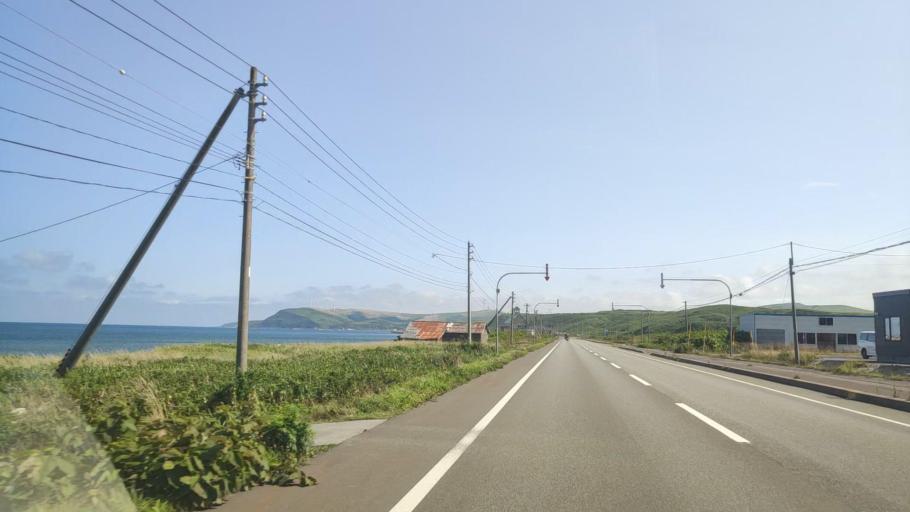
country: JP
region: Hokkaido
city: Makubetsu
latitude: 45.4338
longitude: 141.8580
